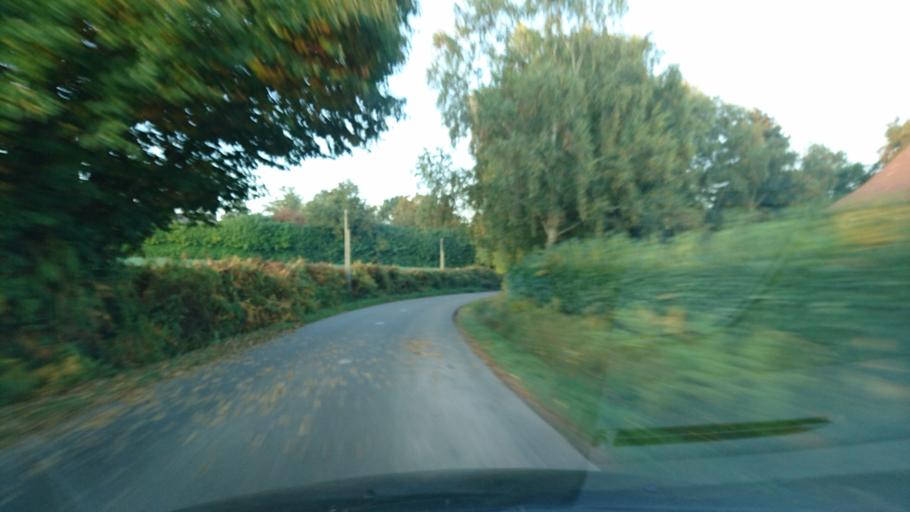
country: FR
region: Brittany
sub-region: Departement d'Ille-et-Vilaine
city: Bruz
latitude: 48.0146
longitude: -1.7592
